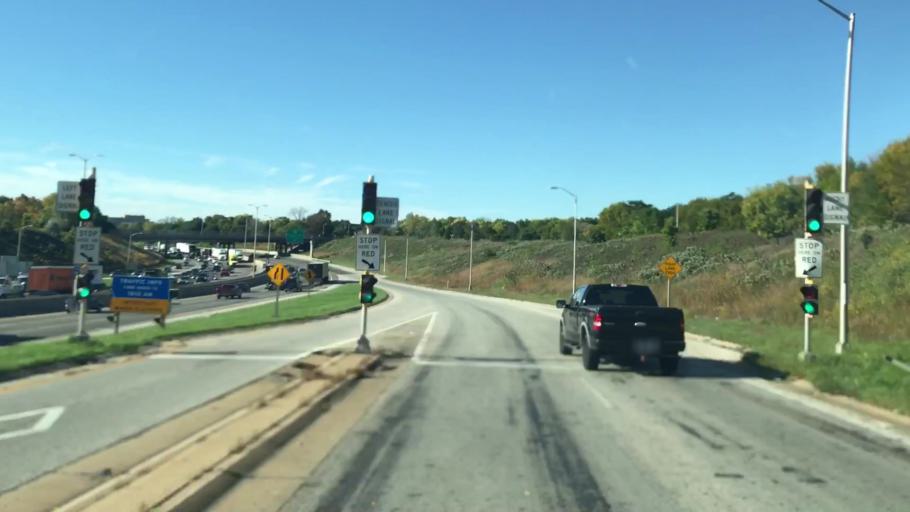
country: US
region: Wisconsin
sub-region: Milwaukee County
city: Milwaukee
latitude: 43.0594
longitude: -87.9227
